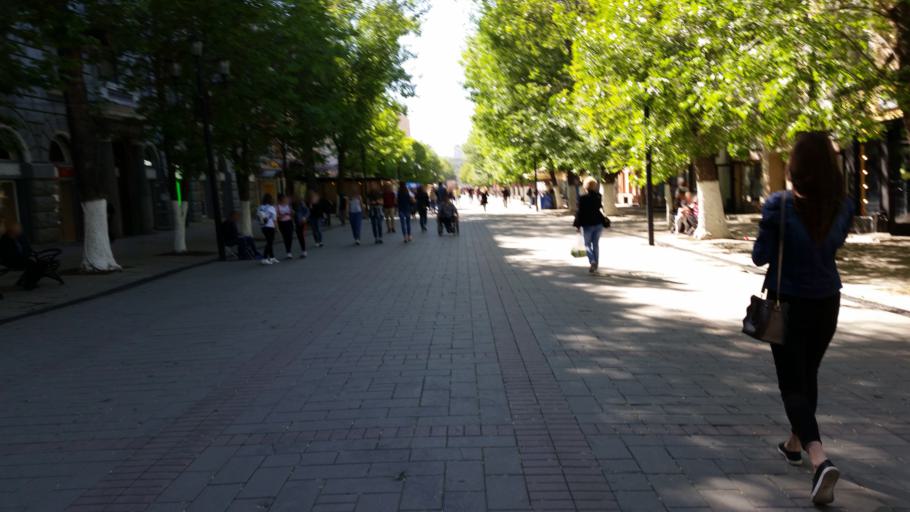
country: RU
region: Saratov
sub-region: Saratovskiy Rayon
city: Saratov
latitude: 51.5313
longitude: 46.0288
